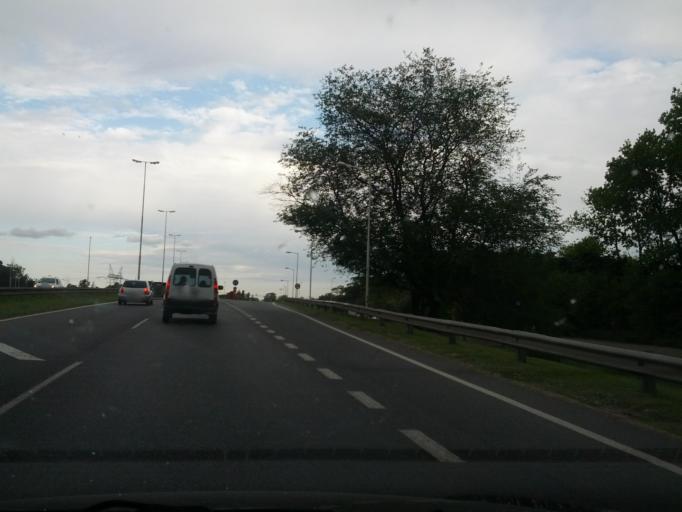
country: AR
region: Buenos Aires
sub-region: Partido de General Rodriguez
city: General Rodriguez
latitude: -34.5779
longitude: -59.0182
